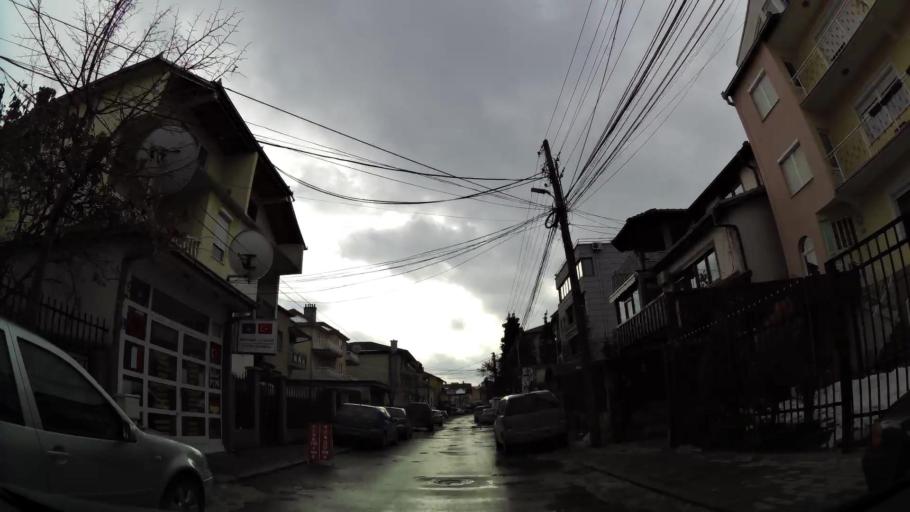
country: XK
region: Pristina
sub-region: Komuna e Prishtines
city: Pristina
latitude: 42.6690
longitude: 21.1544
